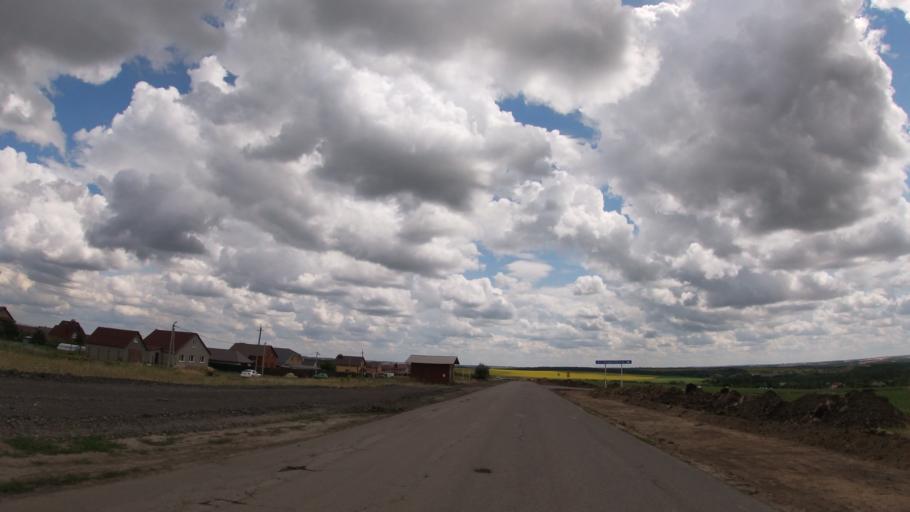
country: RU
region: Belgorod
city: Mayskiy
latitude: 50.5021
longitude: 36.4441
